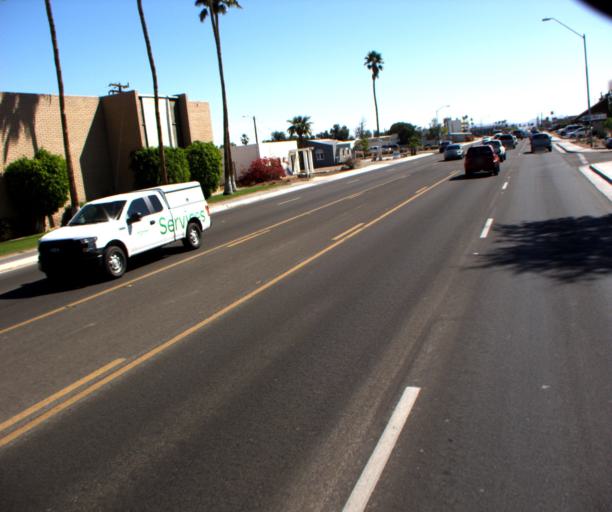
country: US
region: Arizona
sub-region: Yuma County
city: Yuma
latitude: 32.6985
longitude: -114.6295
